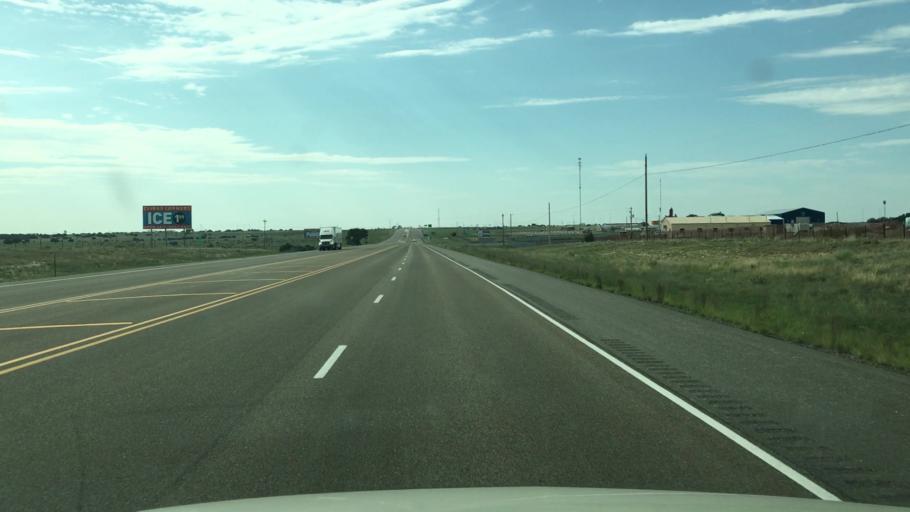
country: US
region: New Mexico
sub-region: Torrance County
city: Moriarty
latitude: 35.0183
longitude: -105.6699
